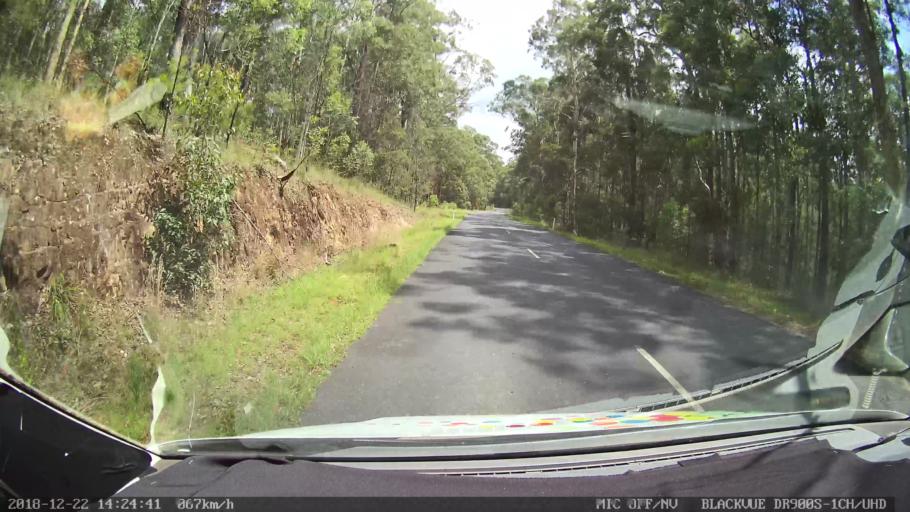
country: AU
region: New South Wales
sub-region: Bellingen
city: Dorrigo
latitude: -30.0457
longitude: 152.6426
